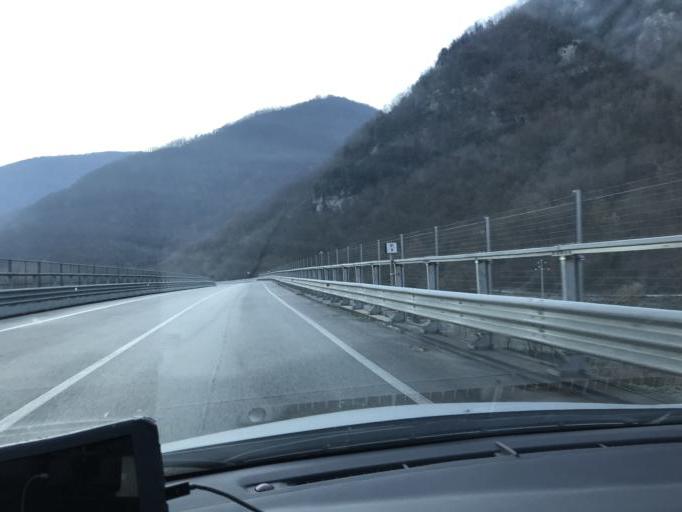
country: IT
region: Latium
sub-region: Provincia di Rieti
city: Cittaducale
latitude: 42.3564
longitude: 12.9370
